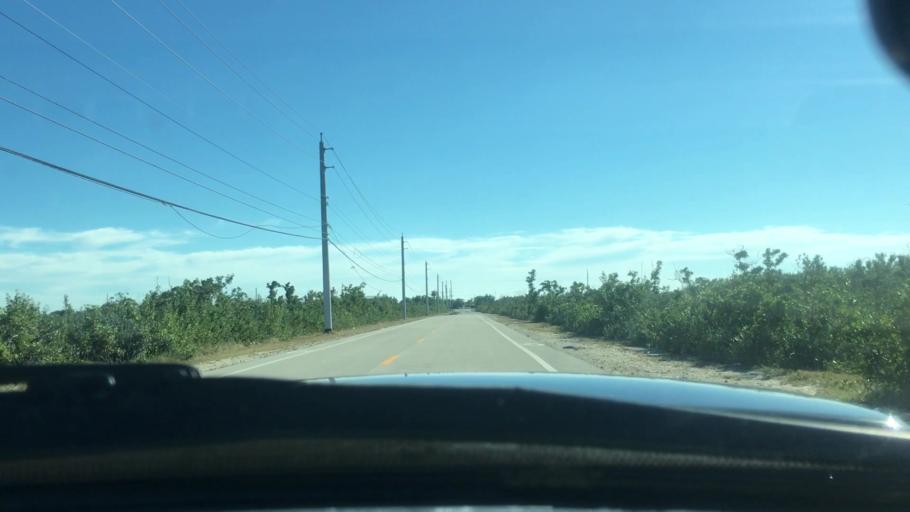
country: US
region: Florida
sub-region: Monroe County
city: Cudjoe Key
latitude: 24.6717
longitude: -81.4997
